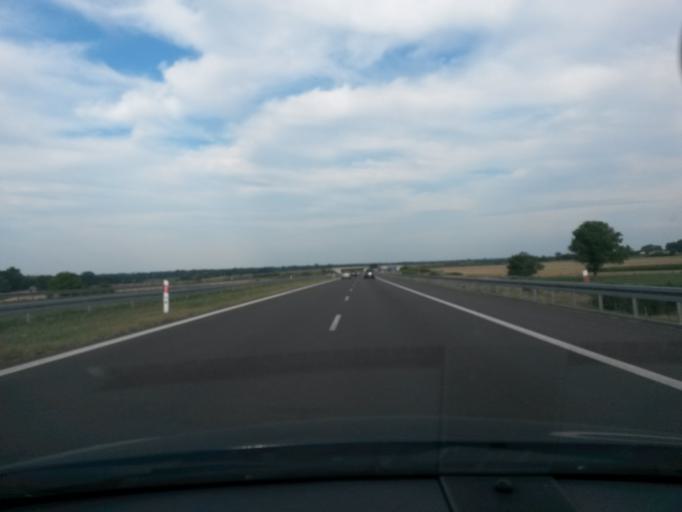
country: PL
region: Greater Poland Voivodeship
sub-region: Powiat kolski
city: Koscielec
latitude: 52.1421
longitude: 18.5811
